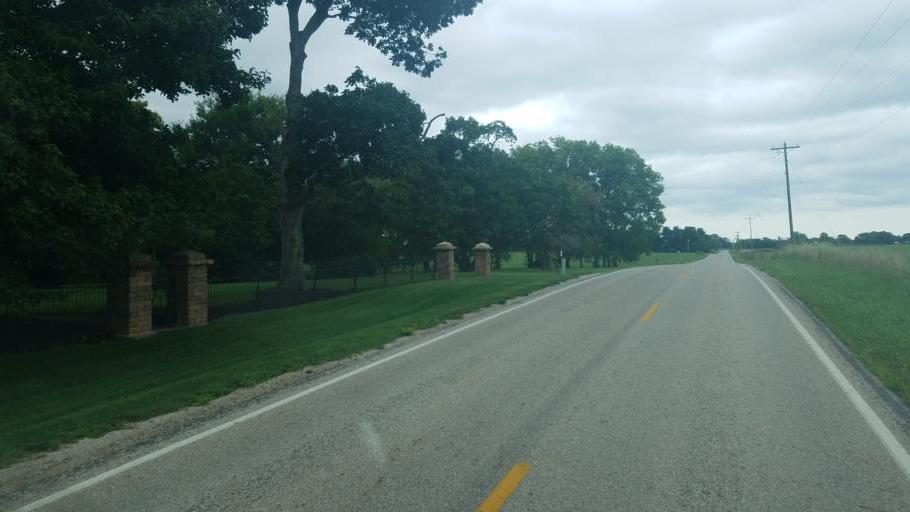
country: US
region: Ohio
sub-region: Pickaway County
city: Circleville
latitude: 39.6429
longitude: -82.9847
